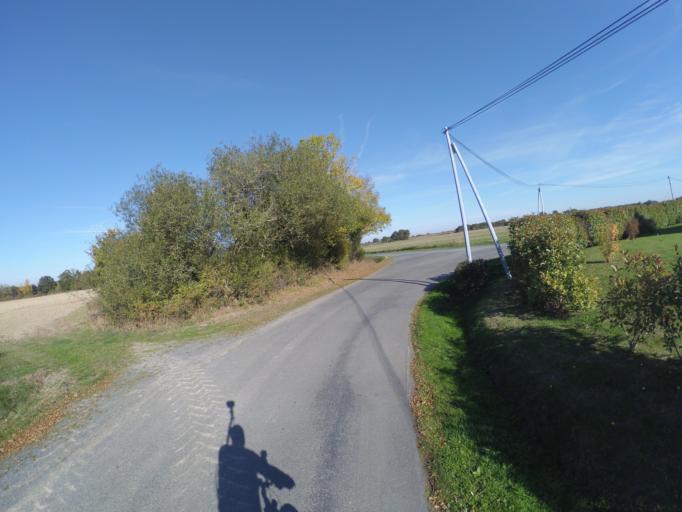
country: FR
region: Pays de la Loire
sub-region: Departement de la Loire-Atlantique
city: Saint-Lumine-de-Clisson
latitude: 47.0599
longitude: -1.3377
